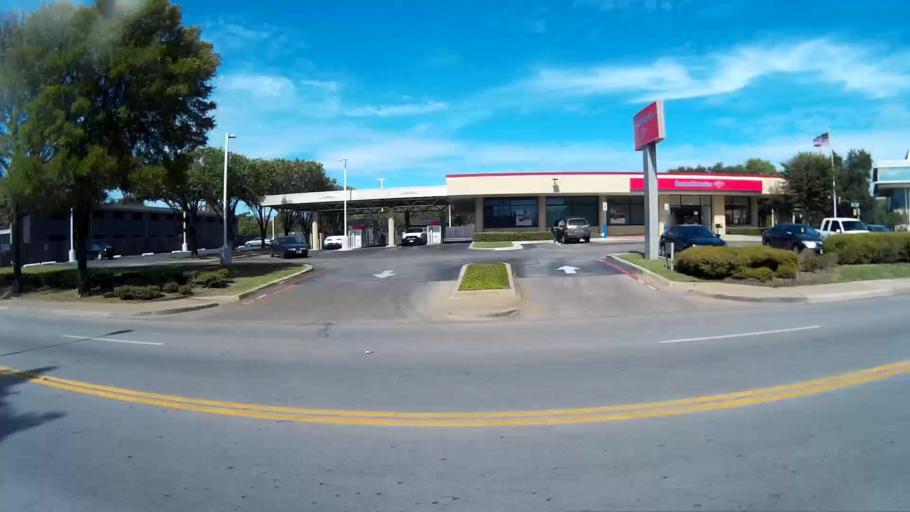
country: US
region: Texas
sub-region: Dallas County
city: Highland Park
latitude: 32.8120
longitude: -96.7552
